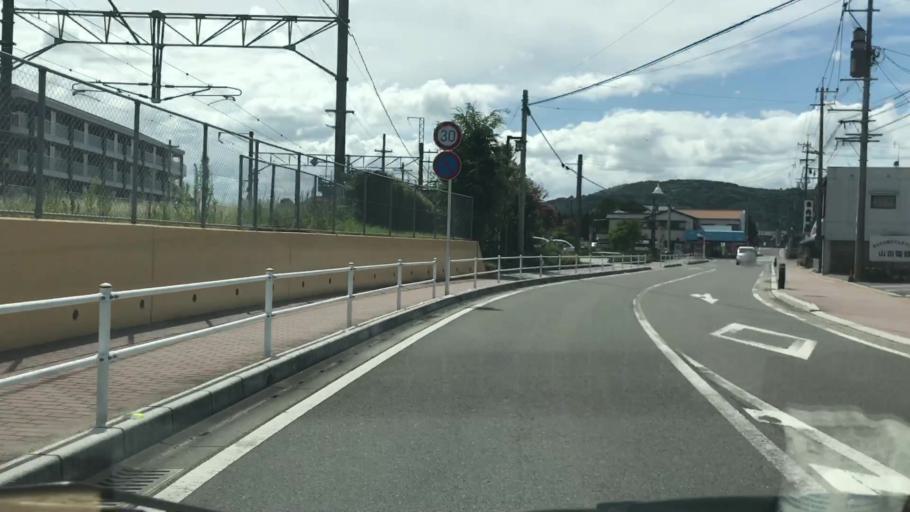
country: JP
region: Saga Prefecture
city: Saga-shi
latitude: 33.2484
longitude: 130.2023
